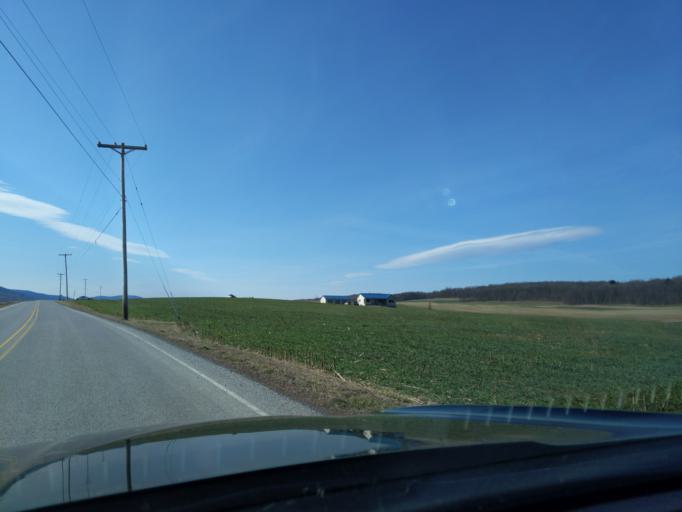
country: US
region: Pennsylvania
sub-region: Blair County
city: Martinsburg
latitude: 40.3574
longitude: -78.2505
